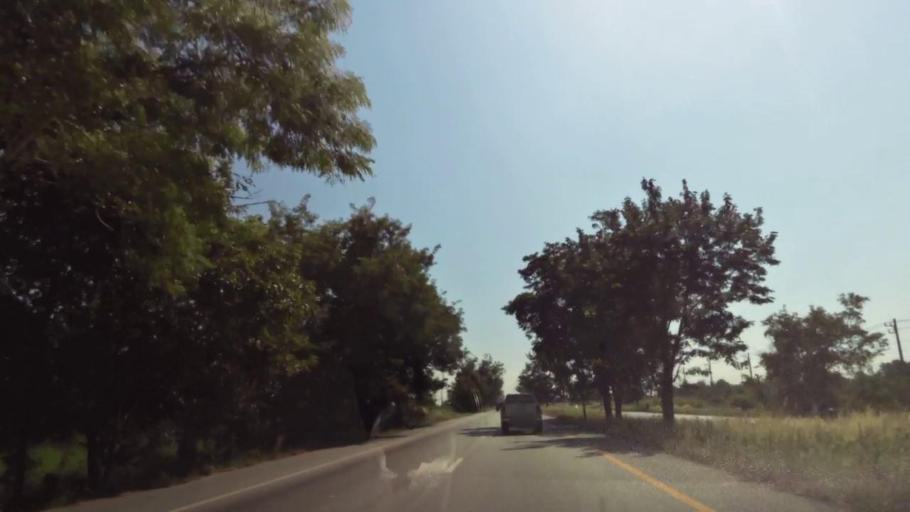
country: TH
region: Nakhon Sawan
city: Kao Liao
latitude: 15.8367
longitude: 100.1176
